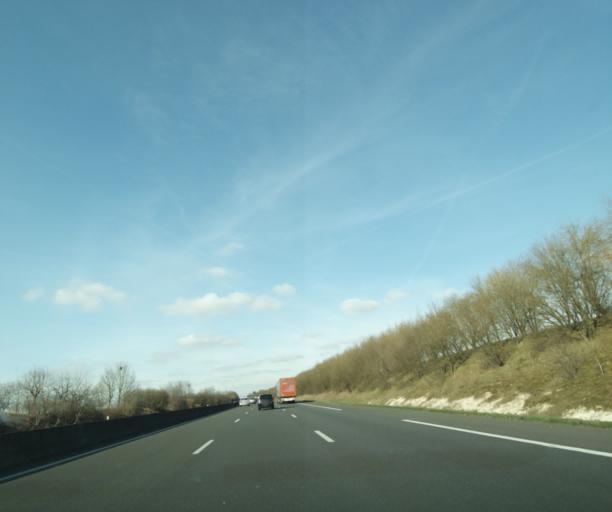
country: FR
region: Centre
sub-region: Departement d'Eure-et-Loir
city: Baigneaux
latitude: 48.1392
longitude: 1.8552
